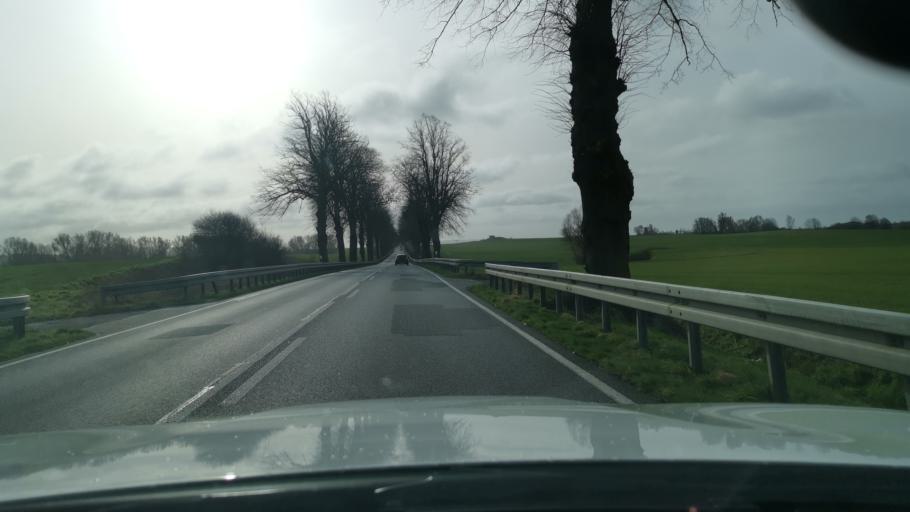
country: DE
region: Mecklenburg-Vorpommern
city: Laage
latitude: 53.9535
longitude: 12.3025
